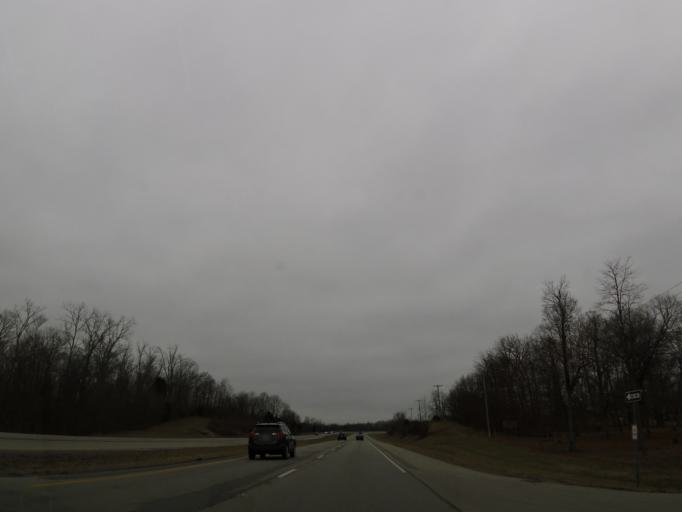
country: US
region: Kentucky
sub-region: Franklin County
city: Frankfort
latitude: 38.1438
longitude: -84.9004
